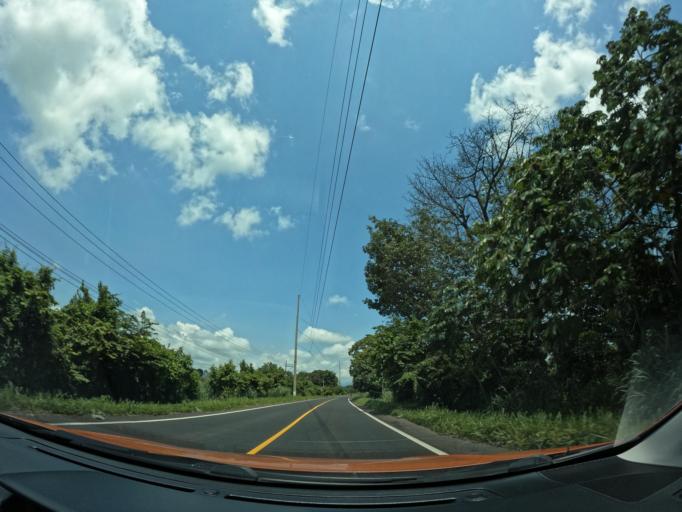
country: GT
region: Escuintla
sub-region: Municipio de Masagua
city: Masagua
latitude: 14.2437
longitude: -90.8133
